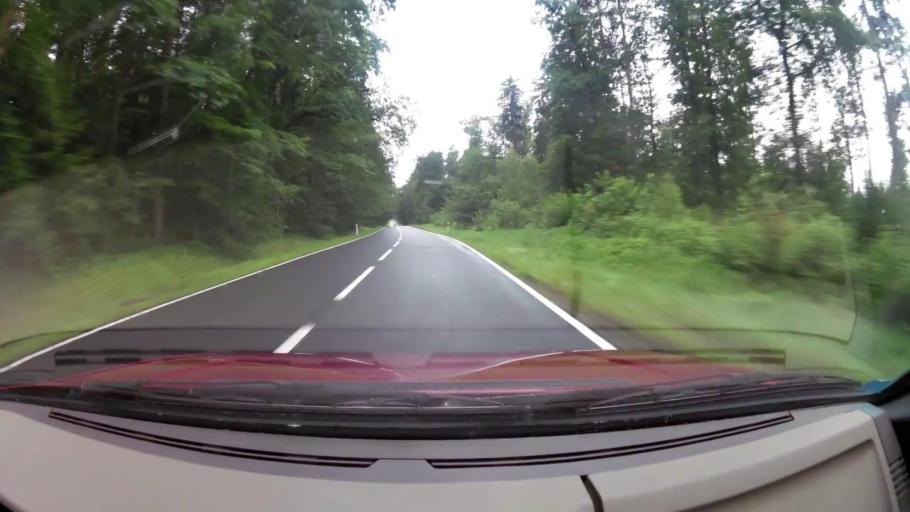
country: PL
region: West Pomeranian Voivodeship
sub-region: Powiat stargardzki
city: Chociwel
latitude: 53.4869
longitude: 15.4066
